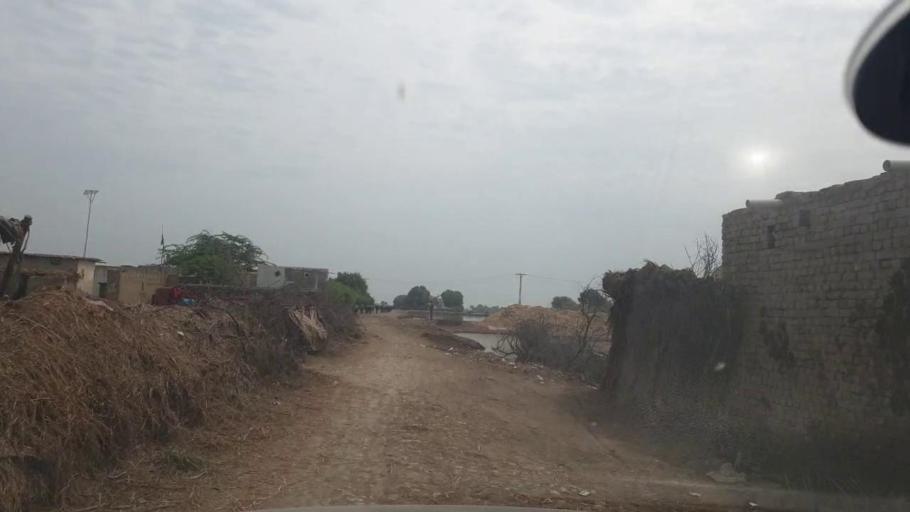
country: PK
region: Sindh
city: Jacobabad
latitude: 28.2411
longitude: 68.5373
